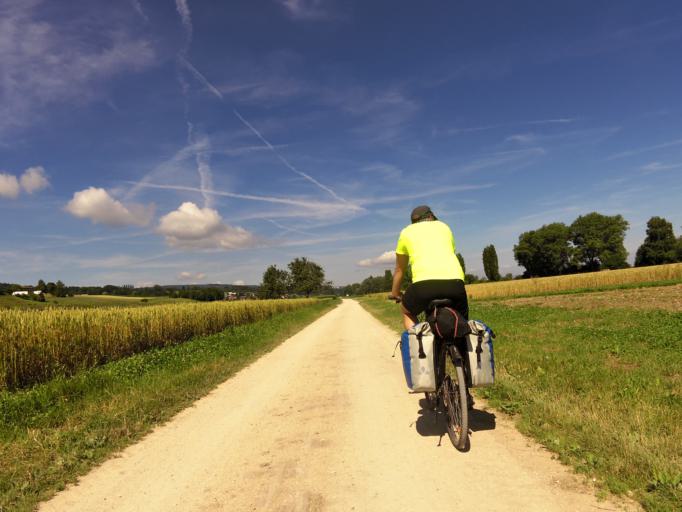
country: CH
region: Thurgau
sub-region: Kreuzlingen District
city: Gottlieben
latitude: 47.6623
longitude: 9.1292
